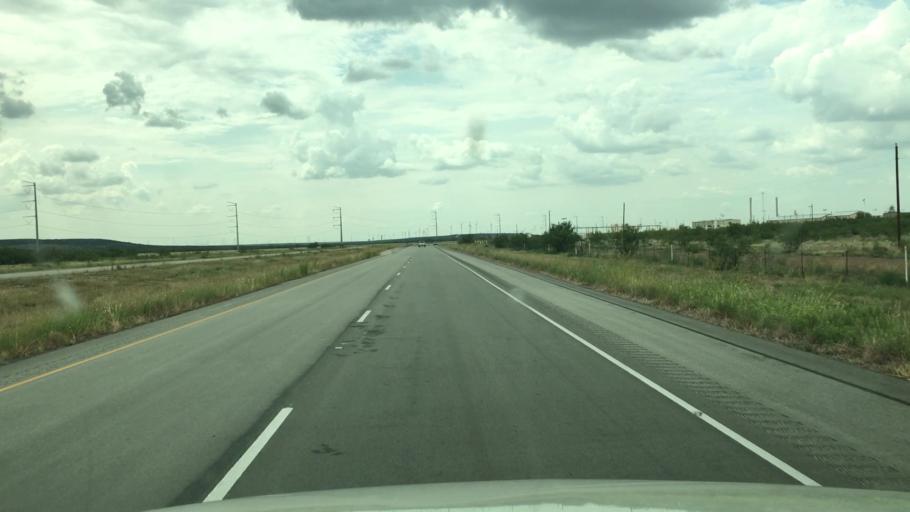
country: US
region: Texas
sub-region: Glasscock County
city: Garden City
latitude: 31.9669
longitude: -101.2329
